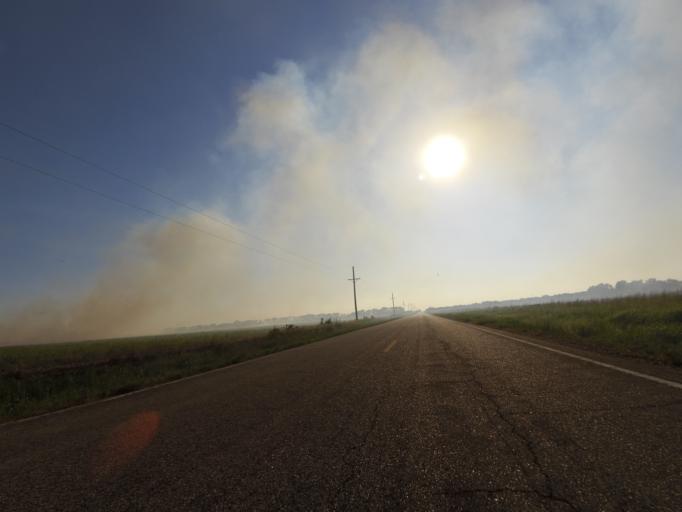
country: US
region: Kansas
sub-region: McPherson County
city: Moundridge
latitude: 38.1451
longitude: -97.5502
